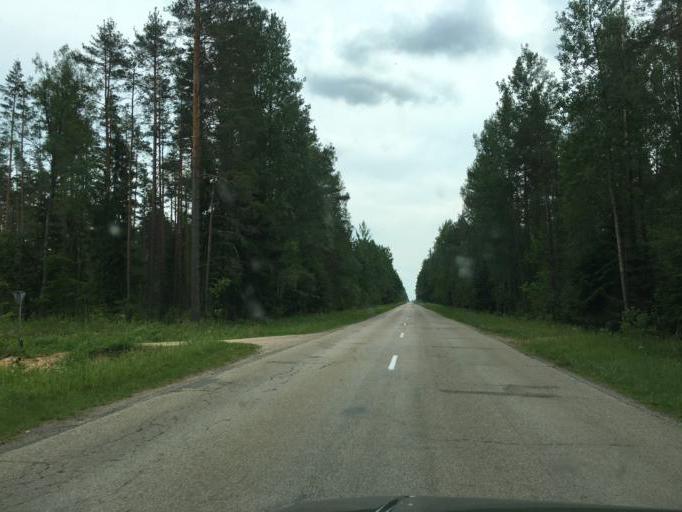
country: LV
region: Rugaju
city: Rugaji
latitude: 56.7850
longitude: 27.1028
